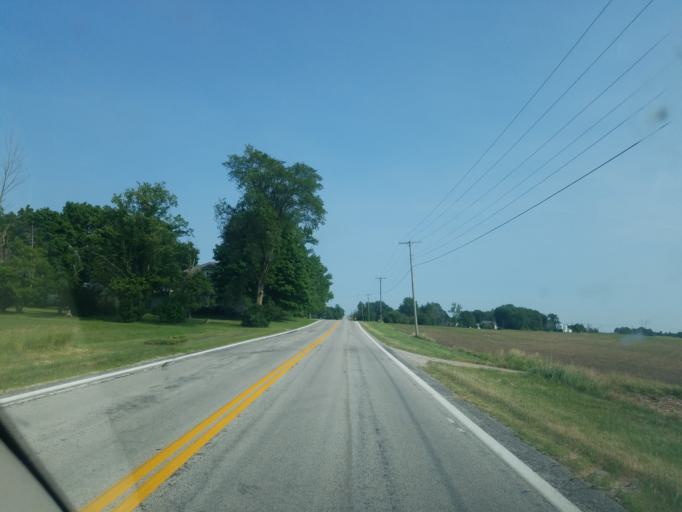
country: US
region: Ohio
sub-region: Wyandot County
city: Carey
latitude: 41.0333
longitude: -83.3022
